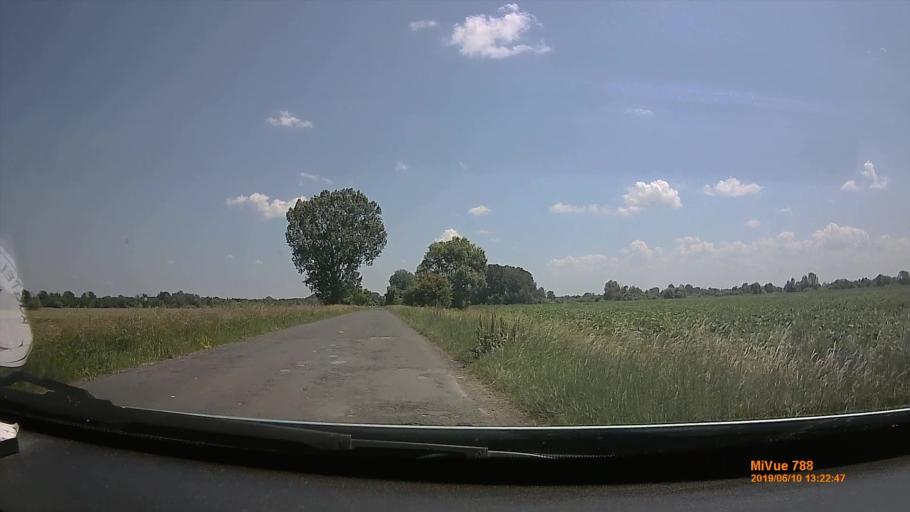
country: HU
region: Borsod-Abauj-Zemplen
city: Tiszaluc
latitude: 48.0287
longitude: 21.0866
